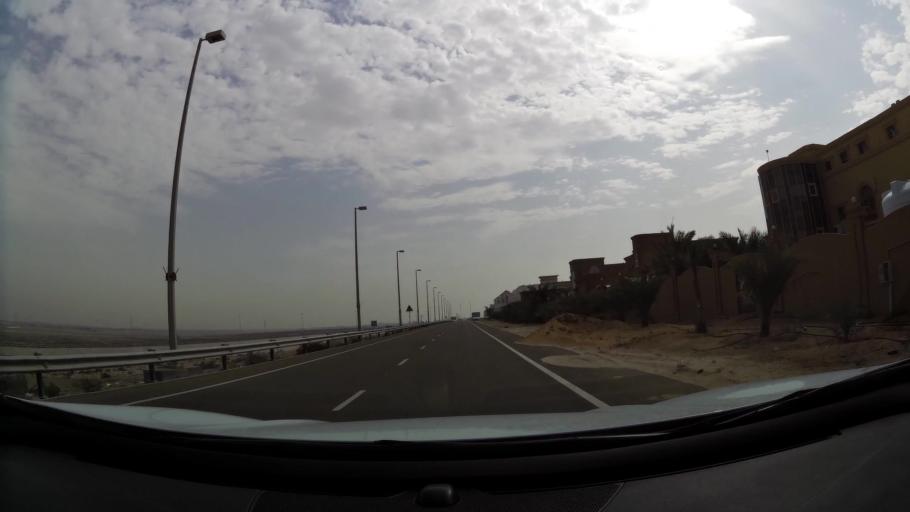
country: AE
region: Abu Dhabi
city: Abu Dhabi
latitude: 24.2766
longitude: 54.6619
